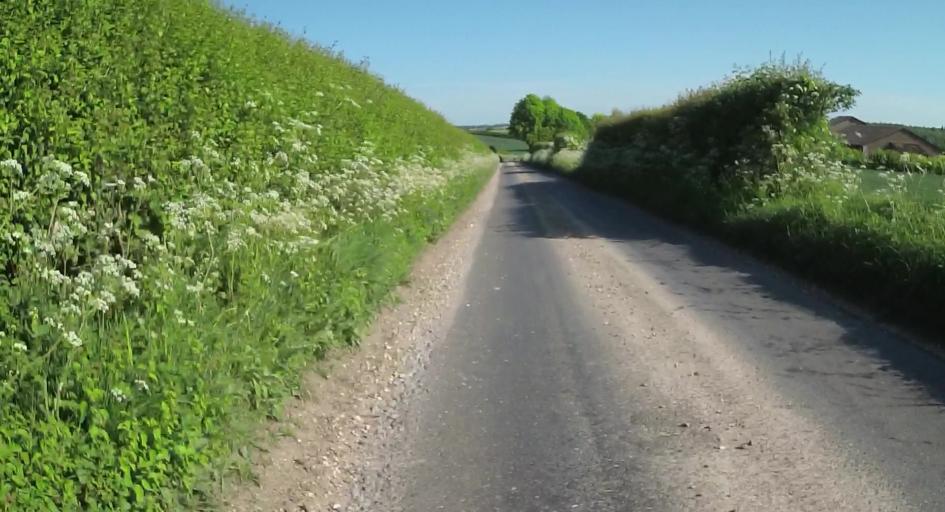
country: GB
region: England
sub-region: Hampshire
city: Overton
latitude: 51.1711
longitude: -1.1959
